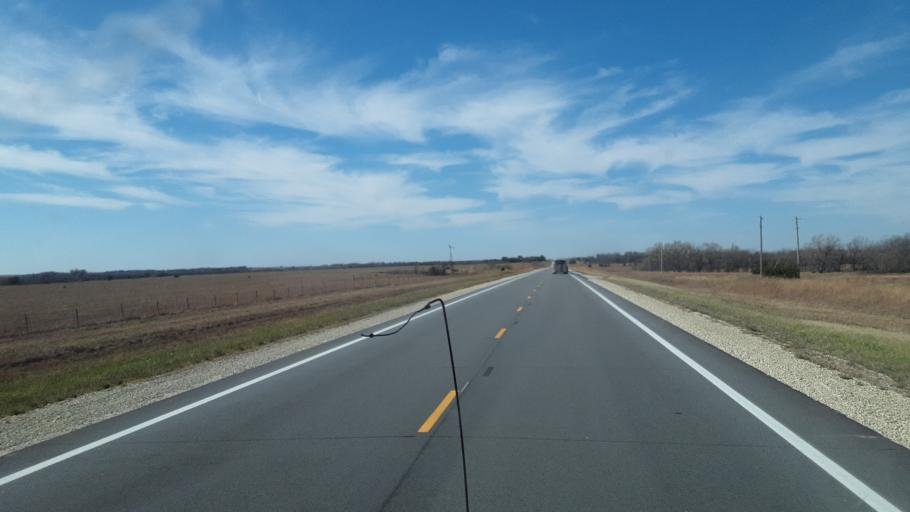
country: US
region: Kansas
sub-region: Marion County
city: Marion
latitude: 38.3627
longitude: -96.8437
